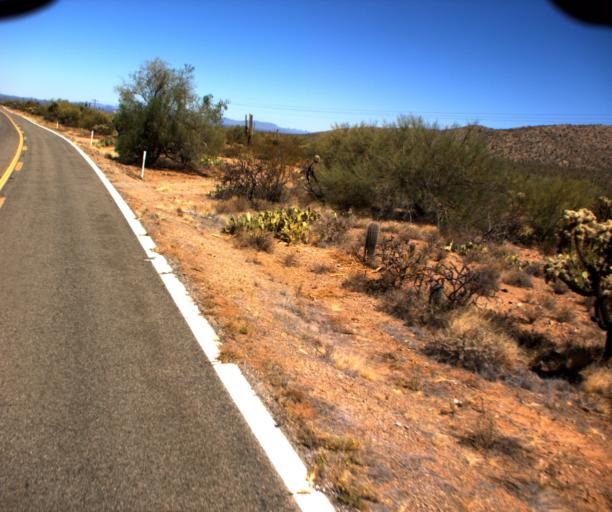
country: US
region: Arizona
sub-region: Pima County
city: Sells
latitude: 32.1757
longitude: -112.2304
